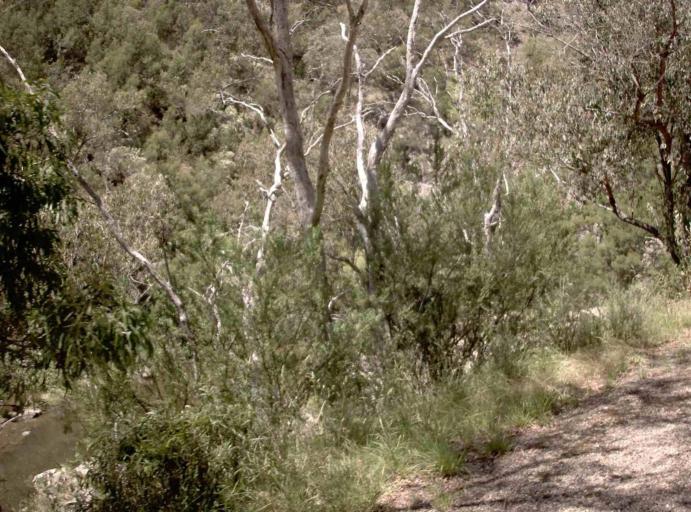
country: AU
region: Victoria
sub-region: East Gippsland
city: Bairnsdale
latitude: -37.4280
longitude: 147.8330
